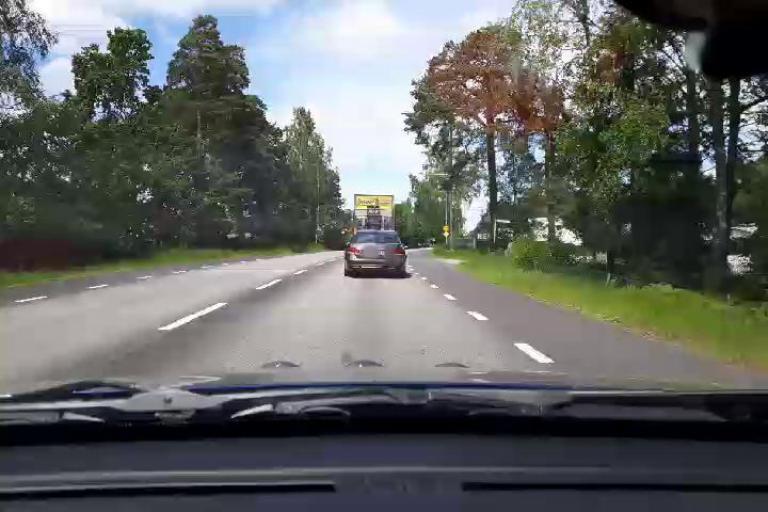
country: SE
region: Uppsala
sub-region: Osthammars Kommun
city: Bjorklinge
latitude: 60.0378
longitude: 17.5506
